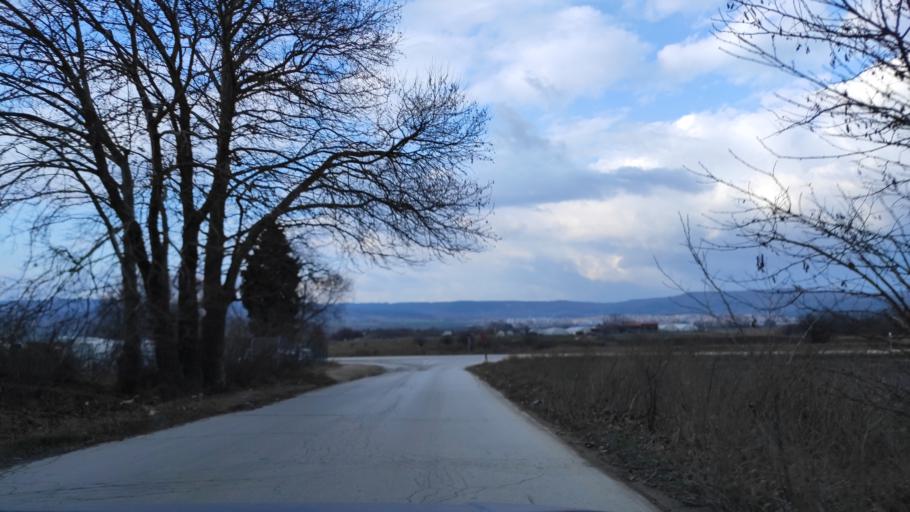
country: BG
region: Varna
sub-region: Obshtina Aksakovo
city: Aksakovo
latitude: 43.2291
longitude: 27.8055
